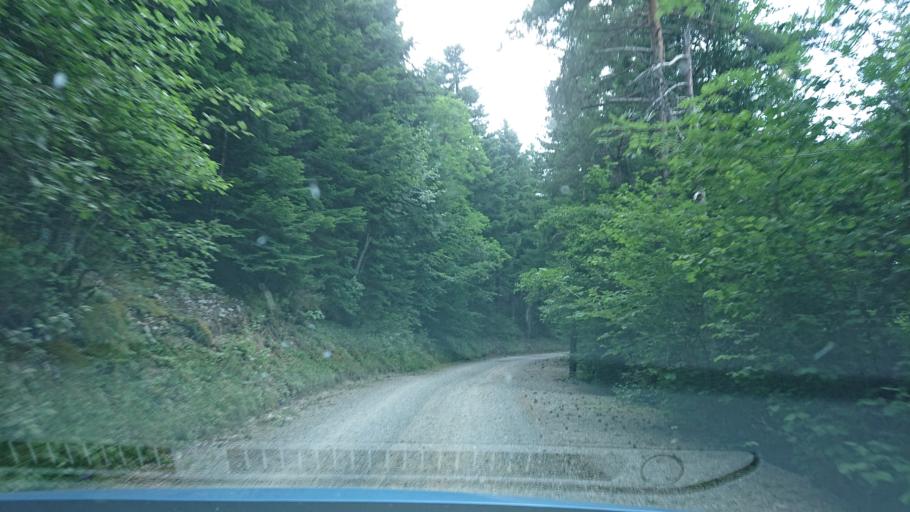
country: FR
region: Rhone-Alpes
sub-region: Departement de l'Isere
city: Mens
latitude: 44.8017
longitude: 5.8897
